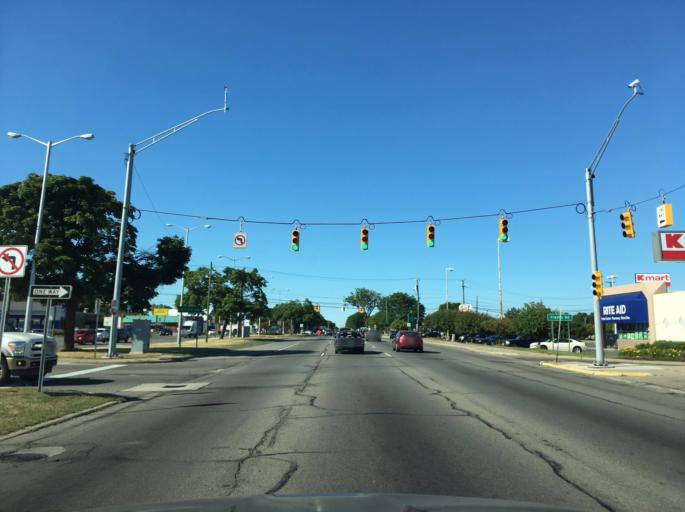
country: US
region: Michigan
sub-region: Macomb County
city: Roseville
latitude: 42.4862
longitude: -82.9436
